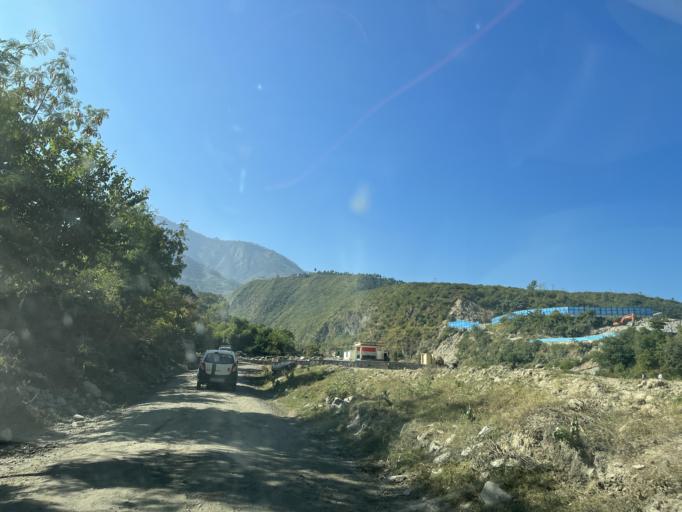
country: IN
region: Uttarakhand
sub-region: Almora
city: Ranikhet
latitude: 29.5507
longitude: 79.4039
